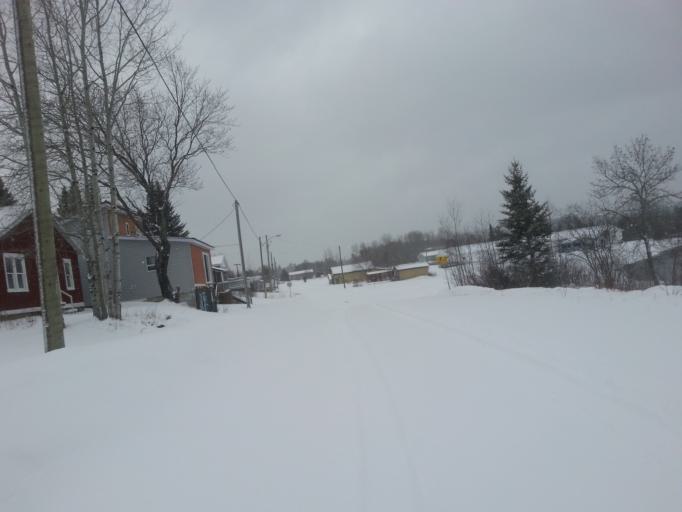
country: CA
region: Ontario
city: Kirkland Lake
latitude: 47.9376
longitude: -80.6510
